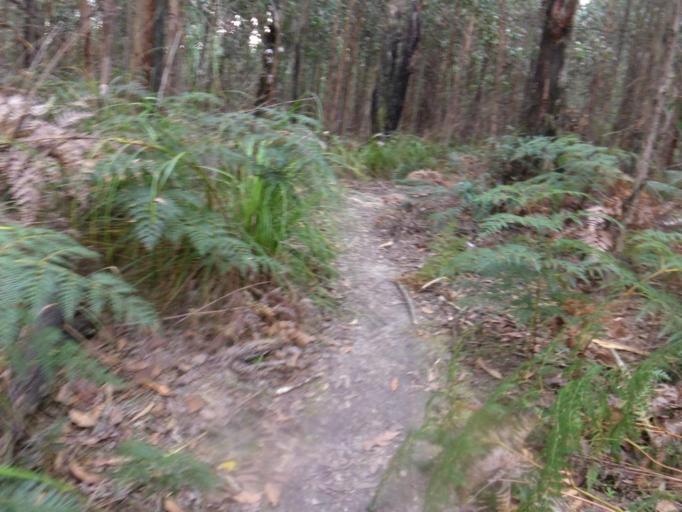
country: AU
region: Victoria
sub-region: Murrindindi
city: Kinglake West
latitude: -37.5184
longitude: 145.2473
